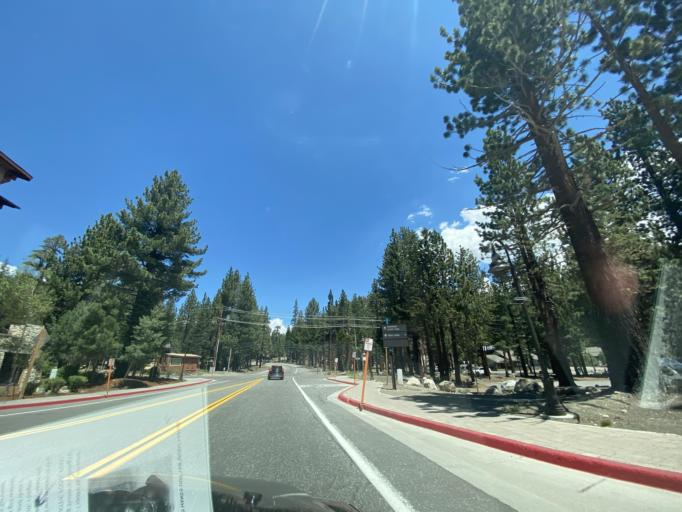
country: US
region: California
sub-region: Mono County
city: Mammoth Lakes
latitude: 37.6516
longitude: -118.9850
